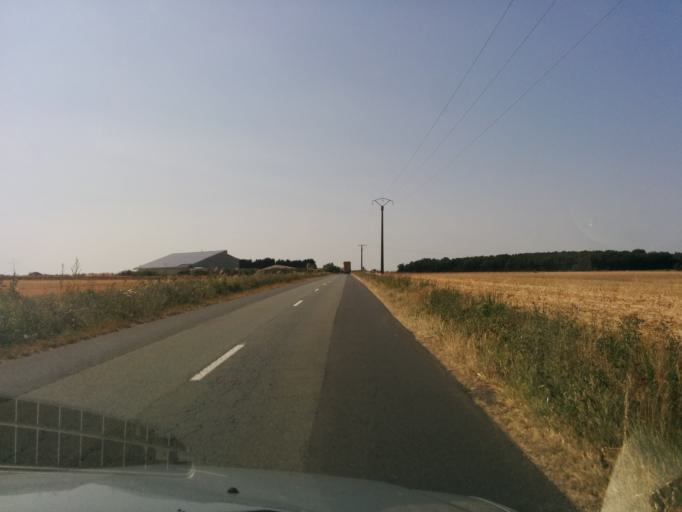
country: FR
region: Poitou-Charentes
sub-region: Departement de la Vienne
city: Mirebeau
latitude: 46.7377
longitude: 0.1867
